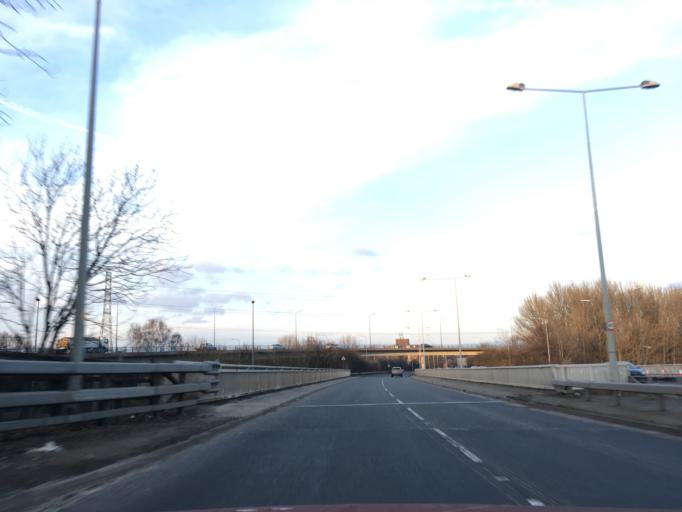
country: GB
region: England
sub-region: Manchester
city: Didsbury
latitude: 53.3982
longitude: -2.2265
